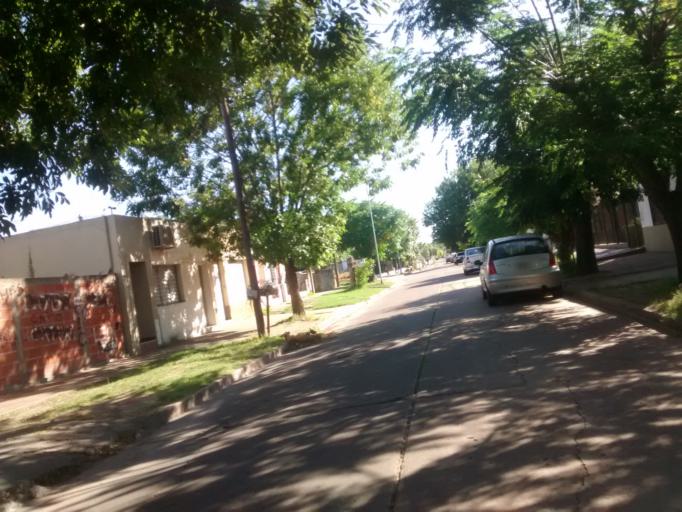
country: AR
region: Buenos Aires
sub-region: Partido de La Plata
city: La Plata
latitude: -34.9355
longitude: -57.9256
